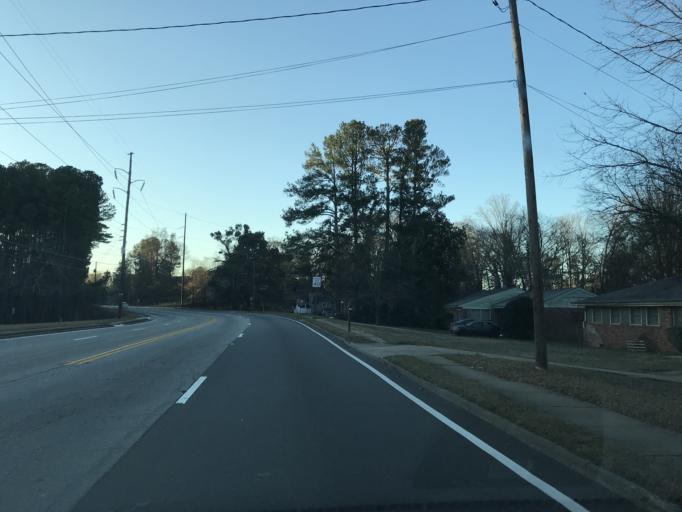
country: US
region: Georgia
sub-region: DeKalb County
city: Tucker
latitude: 33.8749
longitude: -84.2181
